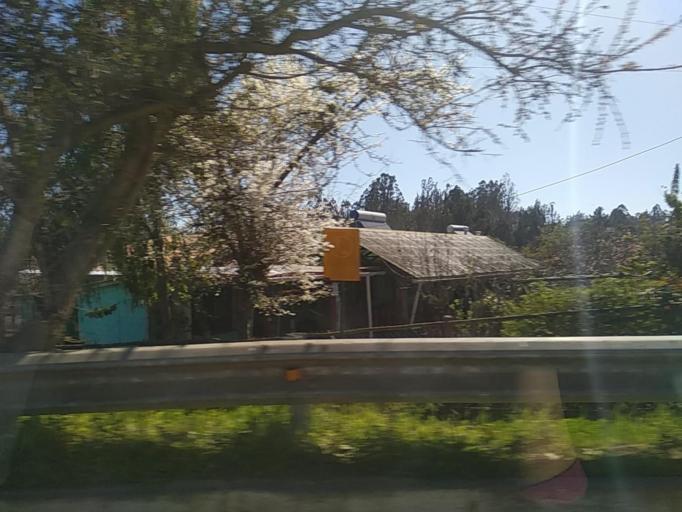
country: CL
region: Valparaiso
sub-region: San Antonio Province
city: El Tabo
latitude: -33.4188
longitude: -71.6251
